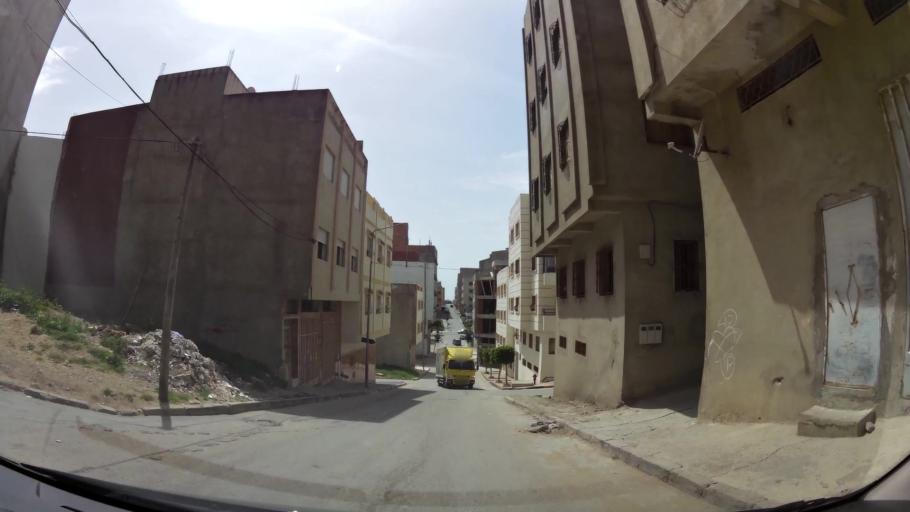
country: MA
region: Tanger-Tetouan
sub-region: Tanger-Assilah
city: Tangier
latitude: 35.7458
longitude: -5.8332
